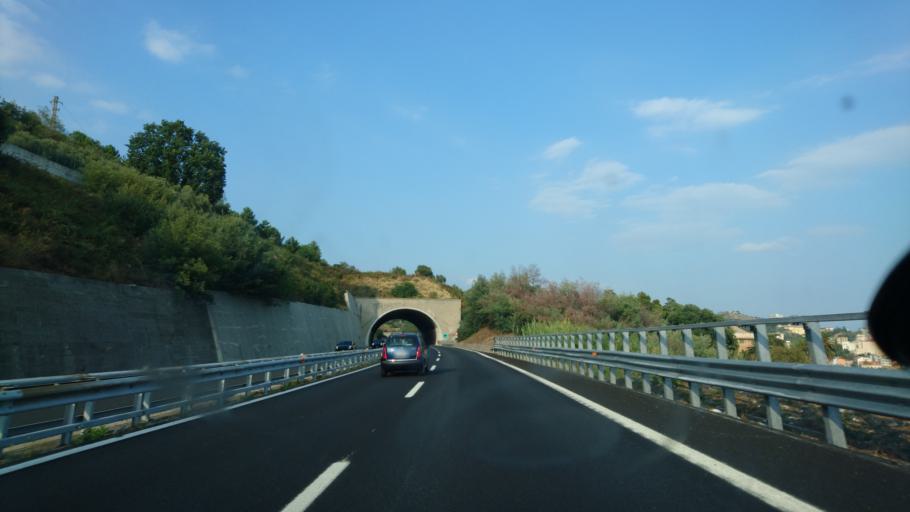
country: IT
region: Liguria
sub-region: Provincia di Savona
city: Savona
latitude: 44.3084
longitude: 8.4653
